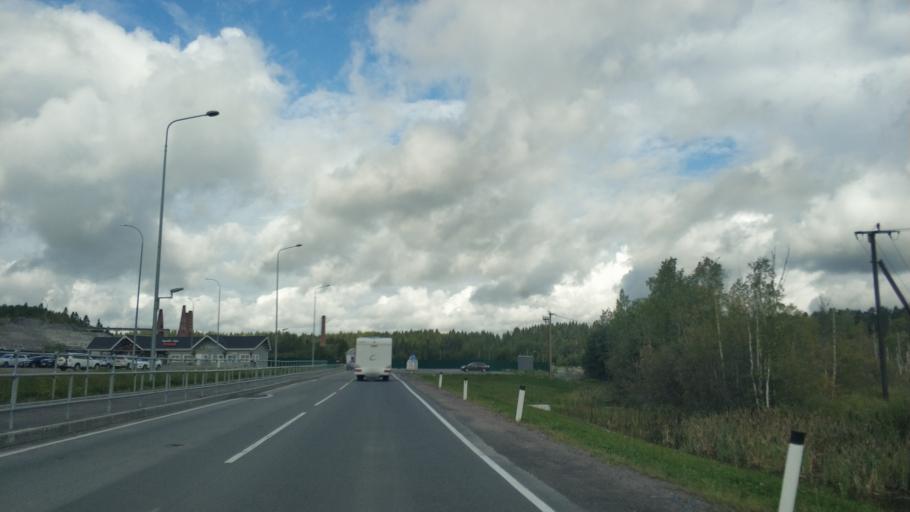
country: RU
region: Republic of Karelia
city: Ruskeala
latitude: 61.9486
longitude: 30.5863
